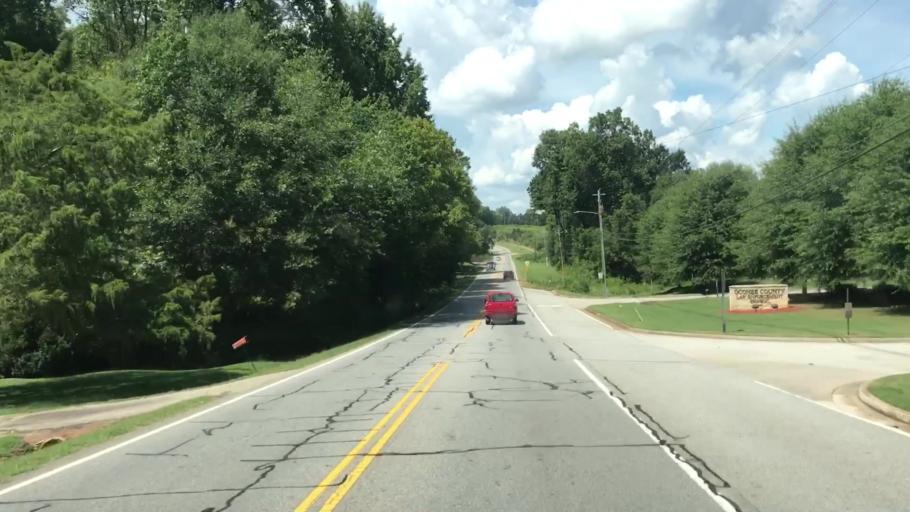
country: US
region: Georgia
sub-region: Oconee County
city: Watkinsville
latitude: 33.8671
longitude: -83.4151
